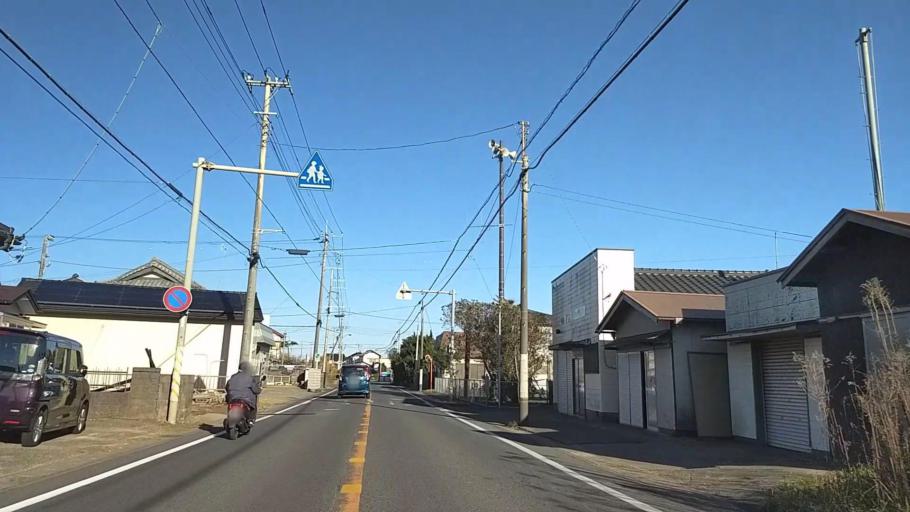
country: JP
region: Chiba
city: Yokaichiba
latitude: 35.6461
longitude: 140.5792
